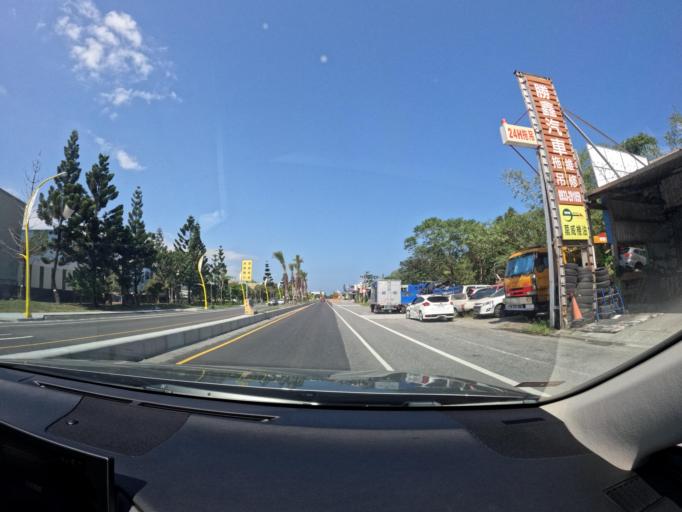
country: TW
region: Taiwan
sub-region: Hualien
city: Hualian
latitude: 23.9273
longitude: 121.5926
